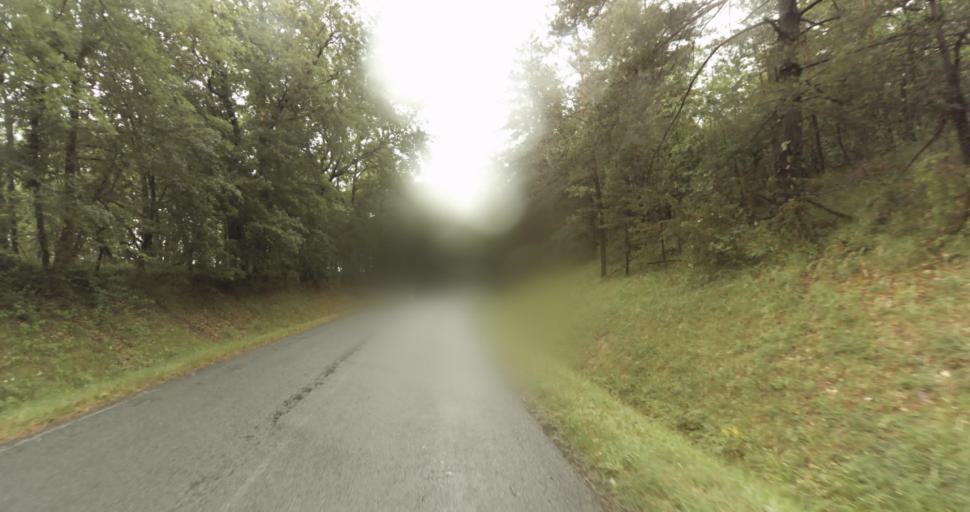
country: FR
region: Aquitaine
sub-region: Departement de la Dordogne
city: Beaumont-du-Perigord
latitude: 44.7983
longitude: 0.8512
